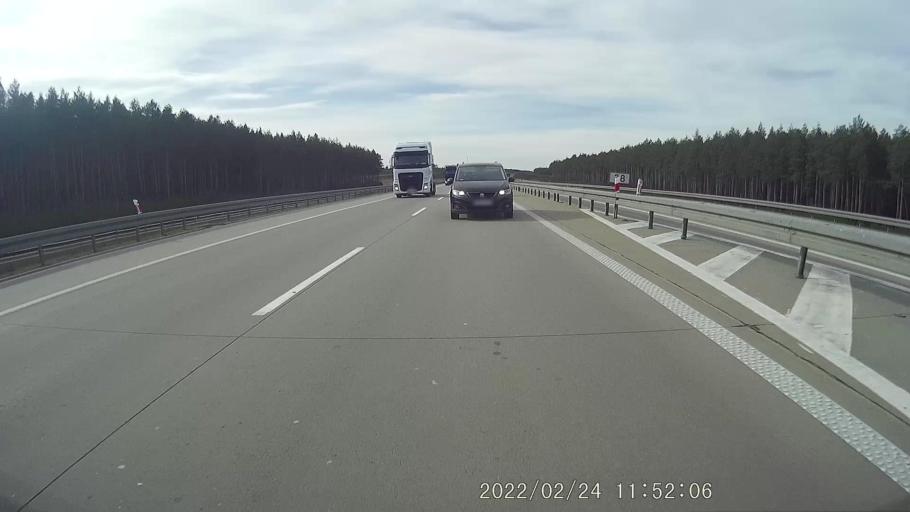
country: PL
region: Lower Silesian Voivodeship
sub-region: Powiat polkowicki
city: Radwanice
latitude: 51.6190
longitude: 15.9732
